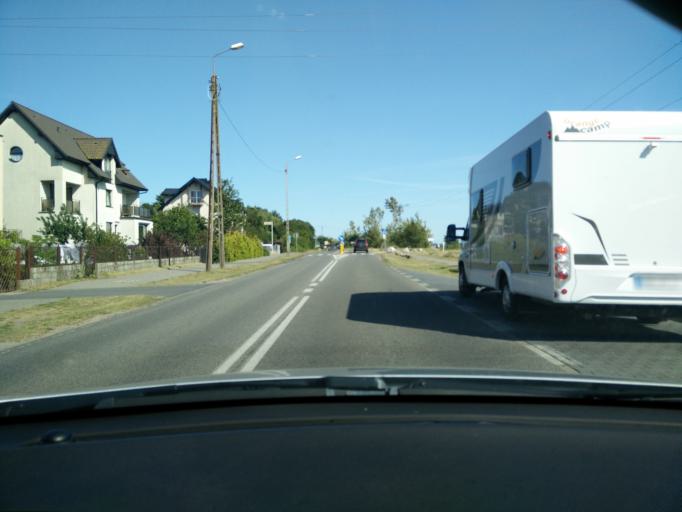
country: PL
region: Pomeranian Voivodeship
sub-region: Powiat pucki
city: Jastarnia
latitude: 54.7284
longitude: 18.5973
